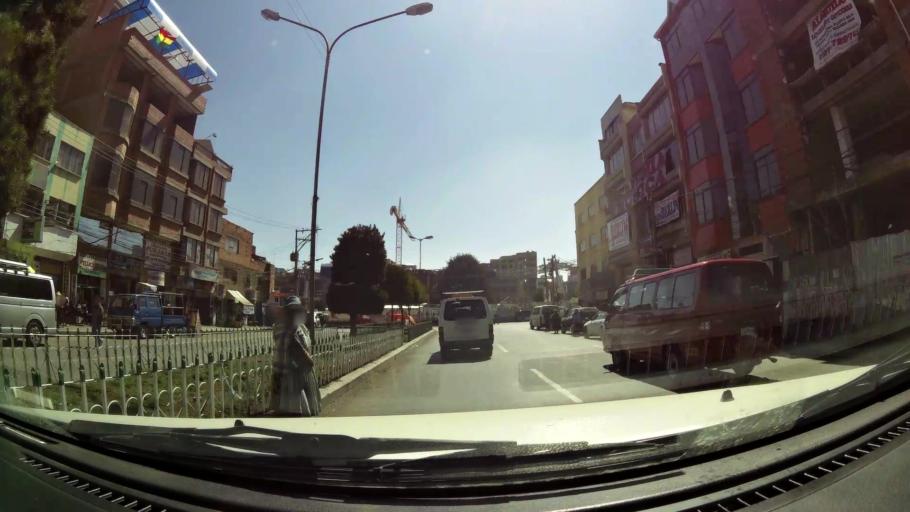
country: BO
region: La Paz
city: La Paz
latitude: -16.4958
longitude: -68.1738
